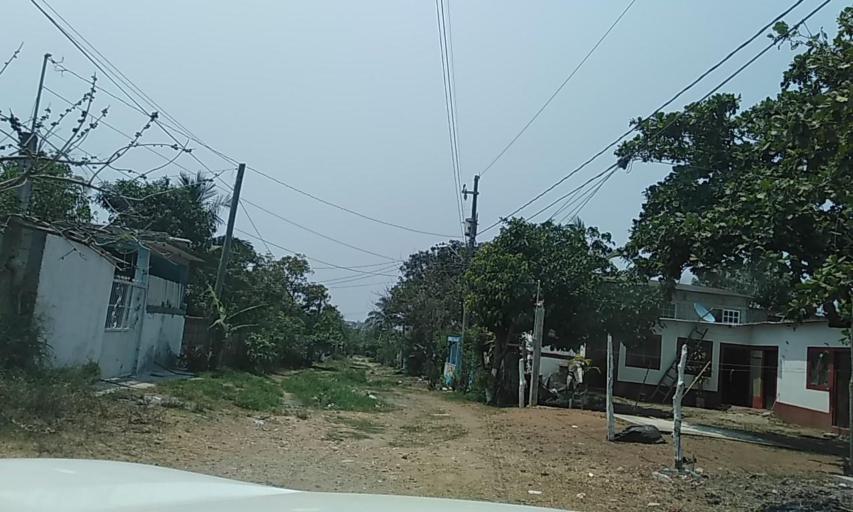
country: MX
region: Veracruz
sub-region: Veracruz
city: Las Amapolas
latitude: 19.1502
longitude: -96.2007
